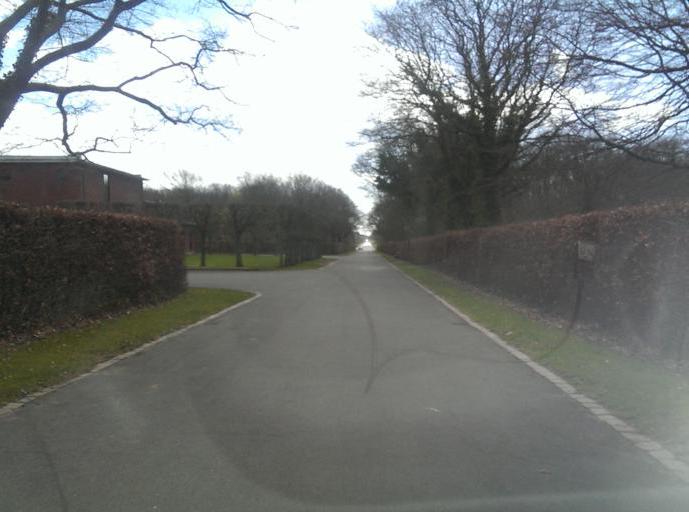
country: DK
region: South Denmark
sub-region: Esbjerg Kommune
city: Esbjerg
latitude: 55.4920
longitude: 8.4143
